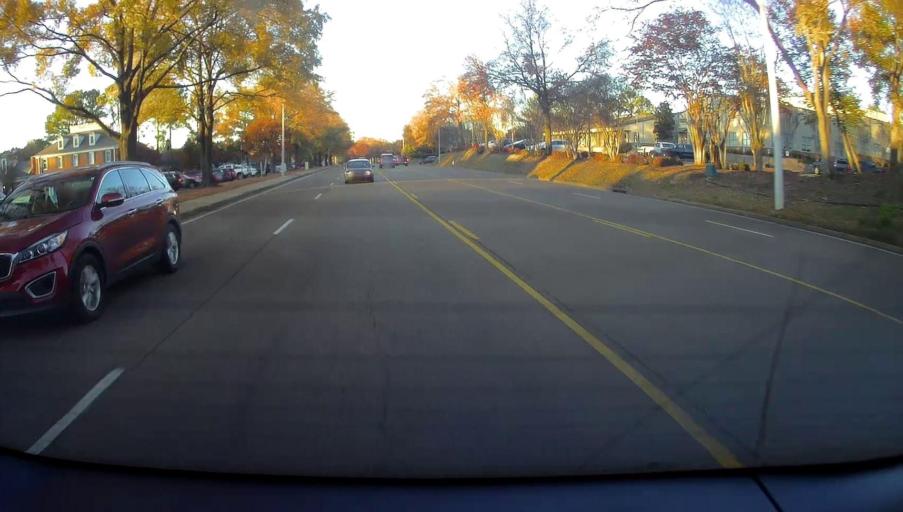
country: US
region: Tennessee
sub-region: Shelby County
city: Germantown
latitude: 35.0894
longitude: -89.8118
